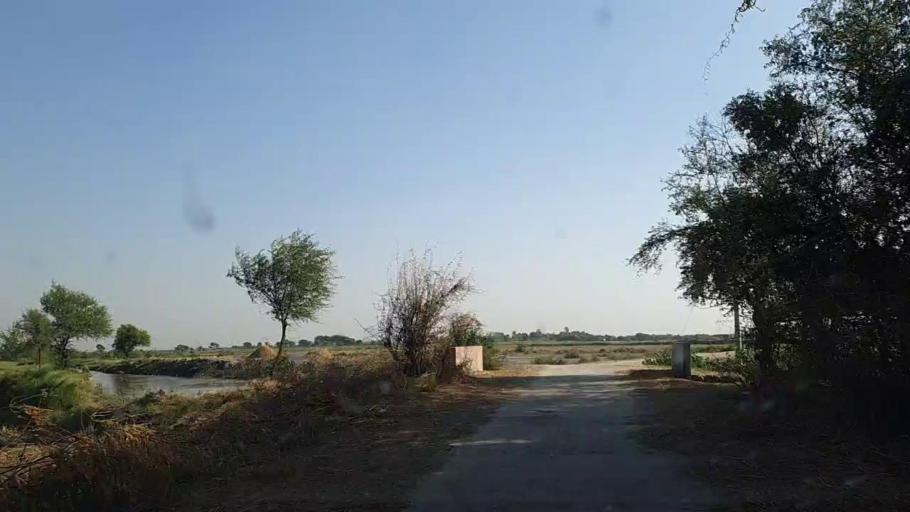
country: PK
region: Sindh
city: Daro Mehar
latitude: 24.6301
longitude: 68.0789
